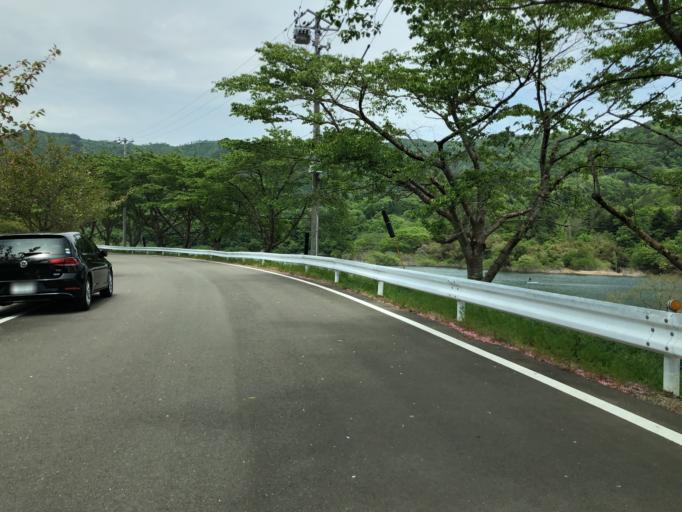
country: JP
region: Miyagi
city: Marumori
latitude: 37.7311
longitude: 140.8088
